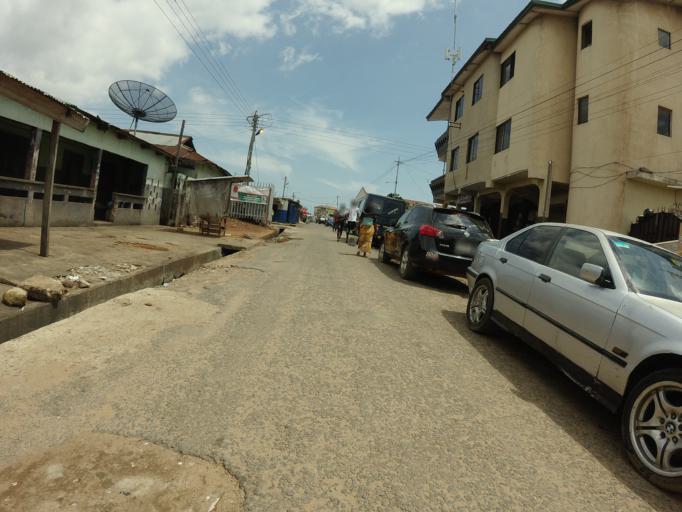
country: GH
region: Greater Accra
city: Accra
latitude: 5.5828
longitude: -0.2010
